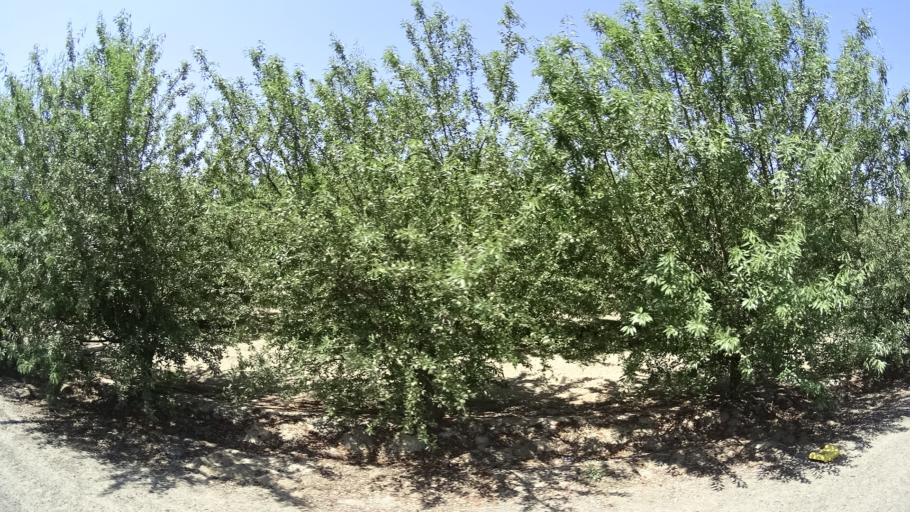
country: US
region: California
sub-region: Kings County
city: Lemoore
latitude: 36.2647
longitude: -119.7630
